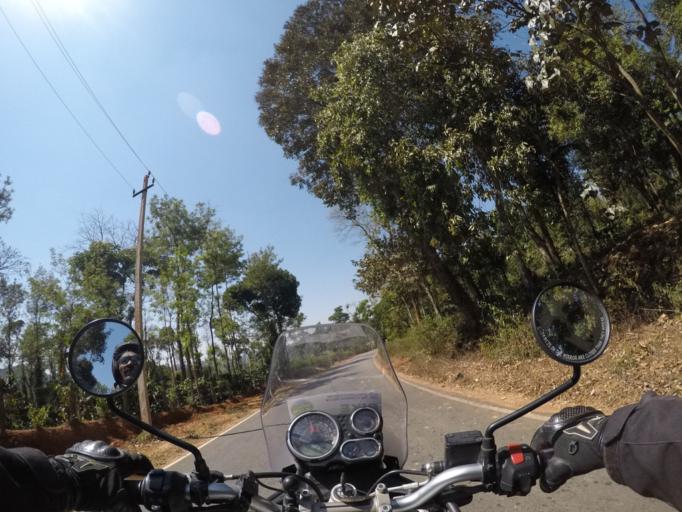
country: IN
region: Karnataka
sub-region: Chikmagalur
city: Mudigere
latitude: 13.0330
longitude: 75.6885
